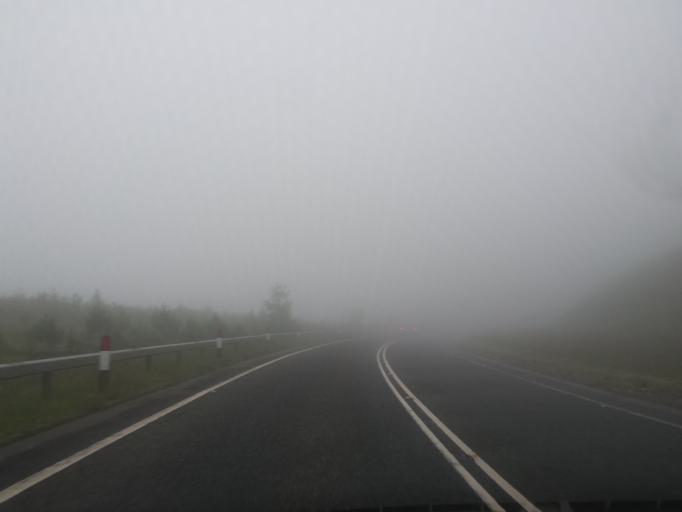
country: GB
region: Scotland
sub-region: Highland
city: Brora
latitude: 58.1391
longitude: -3.6093
